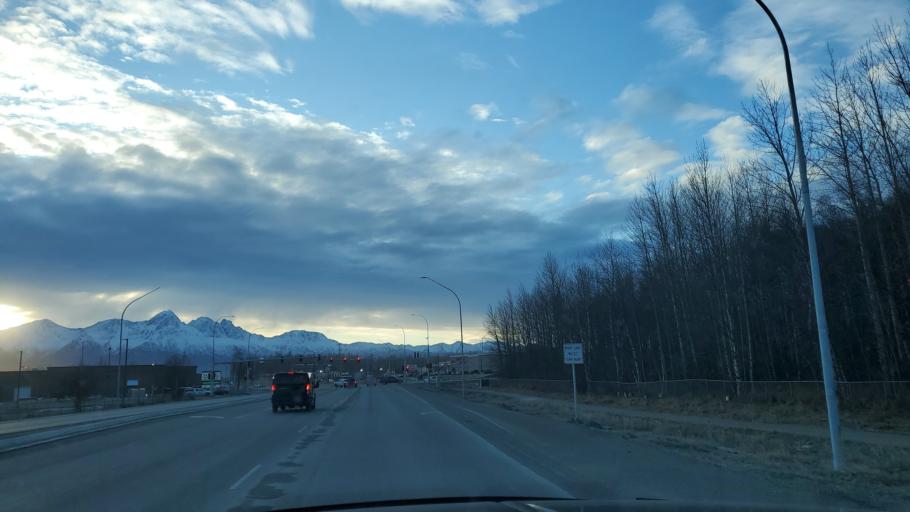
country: US
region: Alaska
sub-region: Matanuska-Susitna Borough
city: Palmer
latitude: 61.6032
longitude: -149.1210
